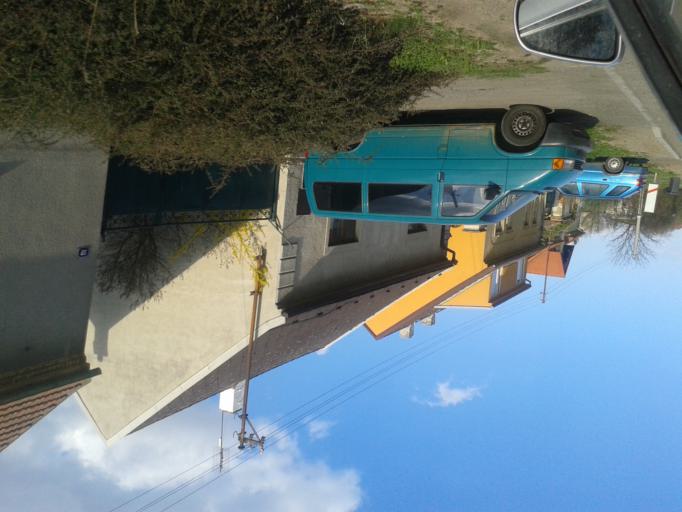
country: CZ
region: Central Bohemia
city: Rudna
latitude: 50.0348
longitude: 14.2342
